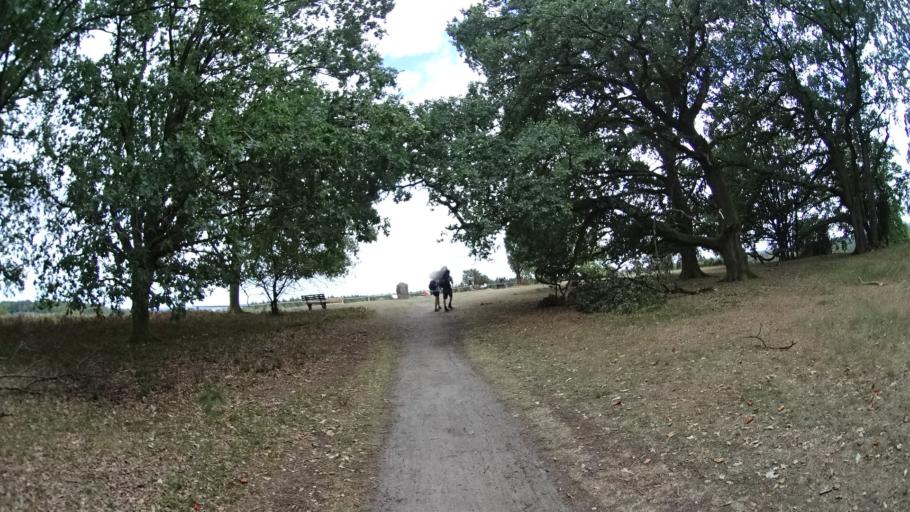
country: DE
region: Lower Saxony
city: Undeloh
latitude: 53.1552
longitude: 9.9672
